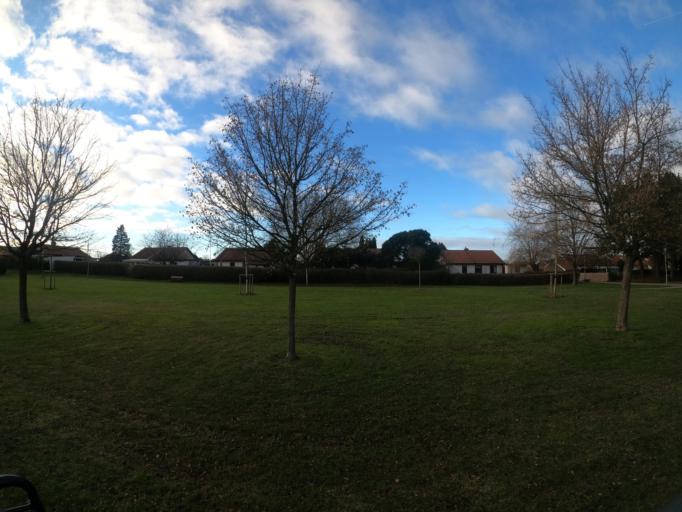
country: SE
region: Skane
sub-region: Svedala Kommun
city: Svedala
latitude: 55.5138
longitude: 13.2375
